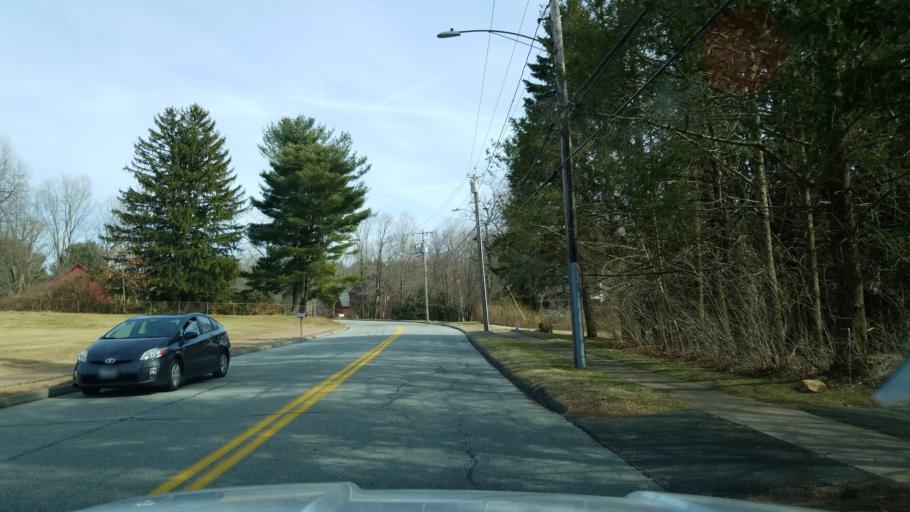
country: US
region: Connecticut
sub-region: Hartford County
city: Glastonbury Center
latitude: 41.7002
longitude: -72.5475
